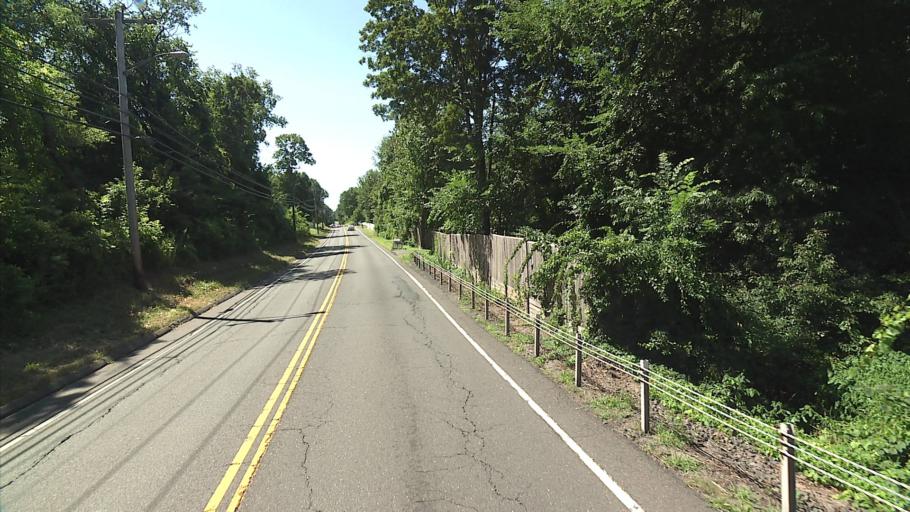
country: US
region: Connecticut
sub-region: Hartford County
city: Farmington
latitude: 41.7683
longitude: -72.8204
